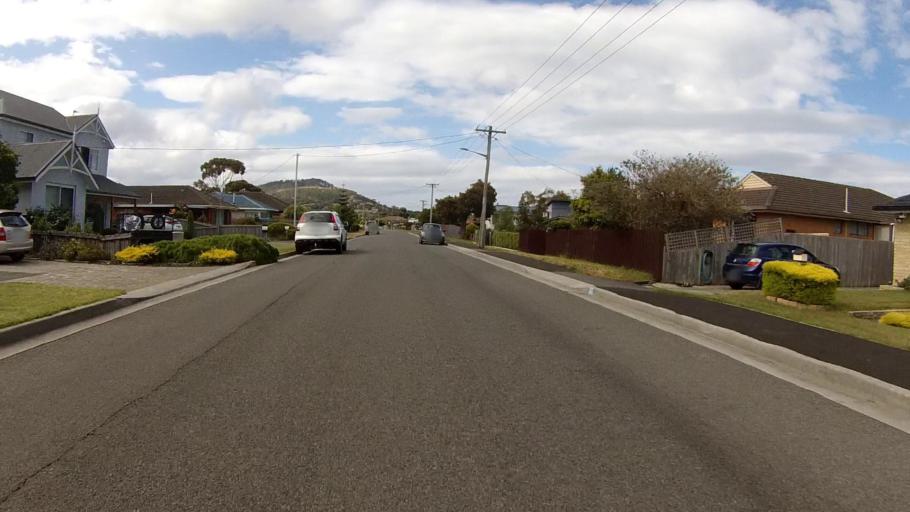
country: AU
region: Tasmania
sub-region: Clarence
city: Lauderdale
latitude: -42.8984
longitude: 147.4947
